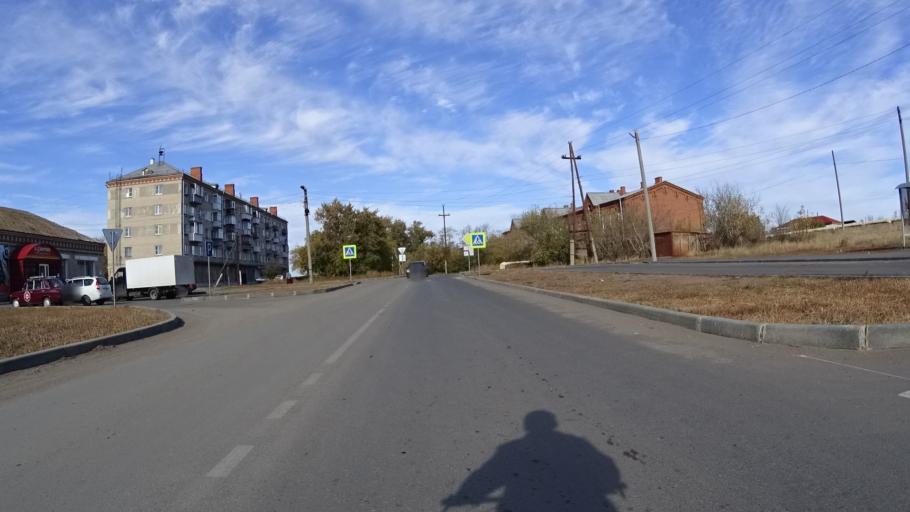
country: RU
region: Chelyabinsk
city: Troitsk
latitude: 54.0776
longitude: 61.5853
